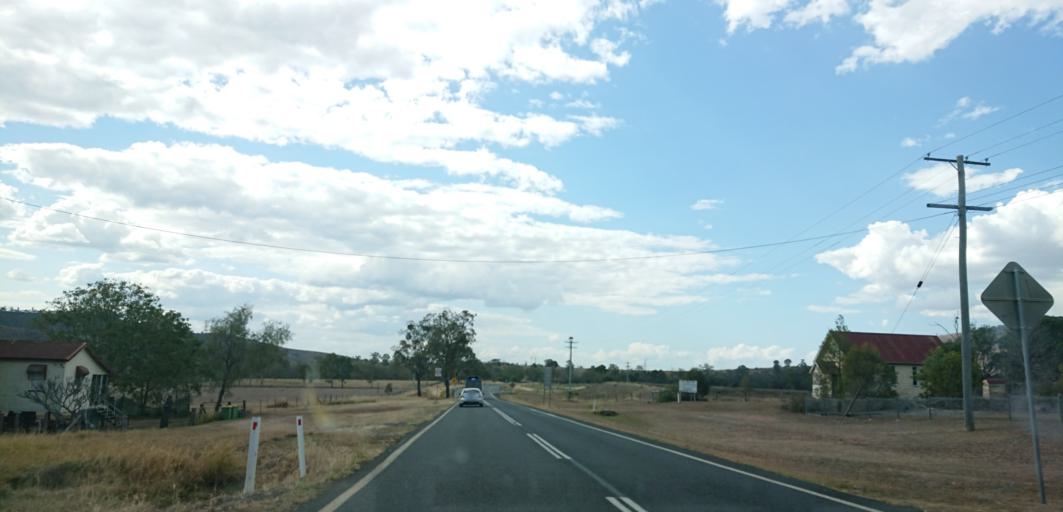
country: AU
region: Queensland
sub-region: Lockyer Valley
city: Gatton
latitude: -27.6649
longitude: 152.1601
